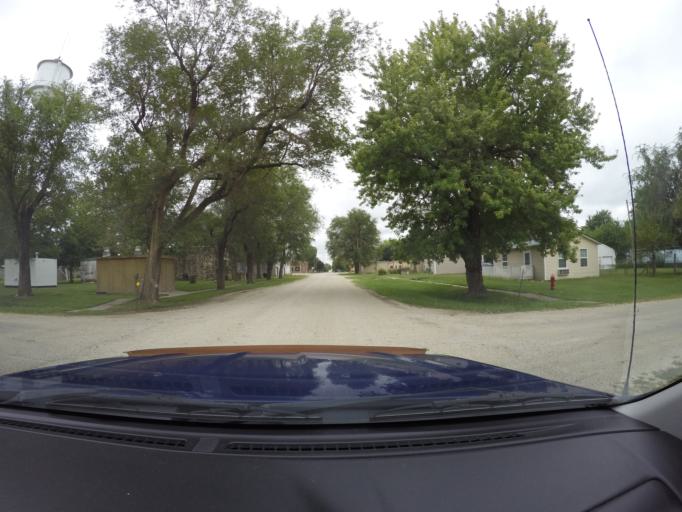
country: US
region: Kansas
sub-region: Geary County
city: Grandview Plaza
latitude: 38.7968
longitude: -96.7357
